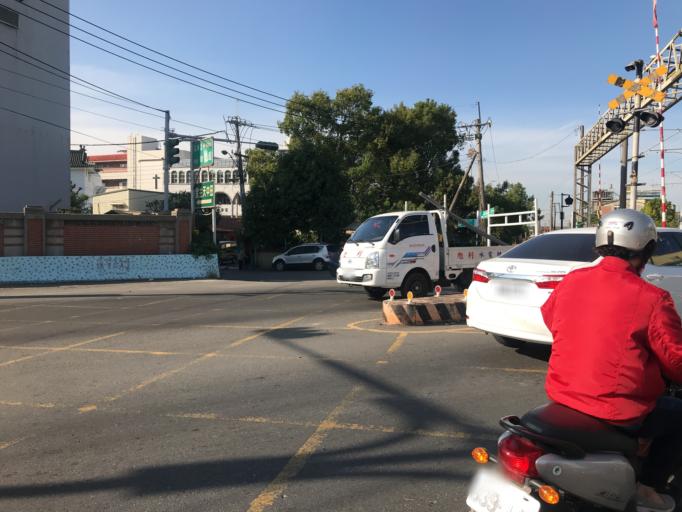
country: TW
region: Taiwan
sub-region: Nantou
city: Nantou
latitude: 23.8679
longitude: 120.5875
